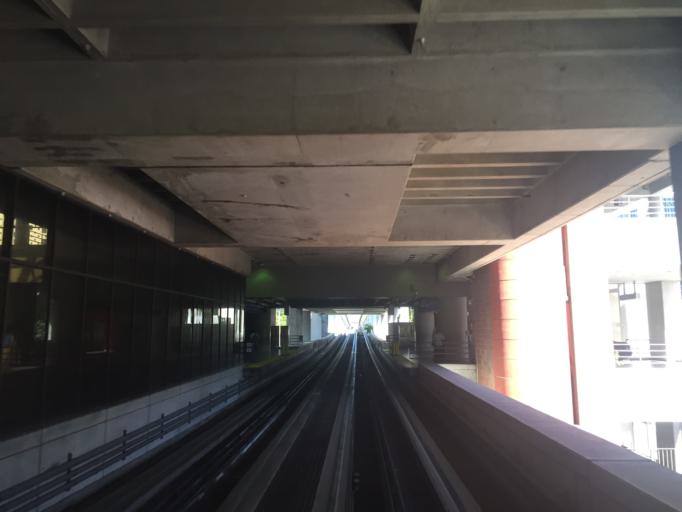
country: US
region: Florida
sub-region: Miami-Dade County
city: Miami
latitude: 25.7755
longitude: -80.1960
